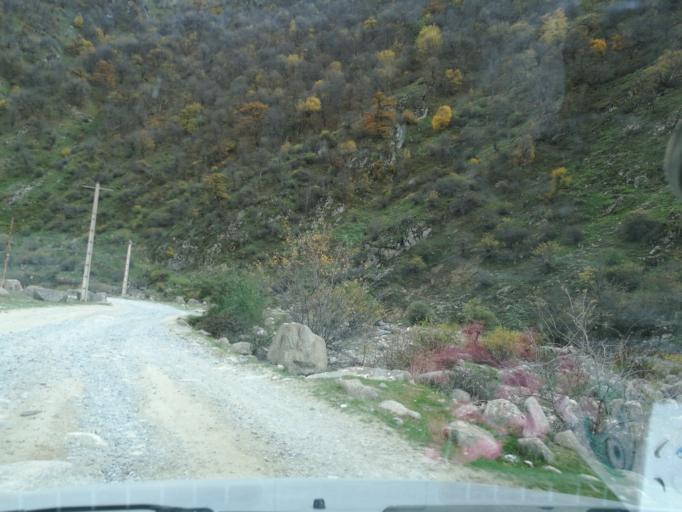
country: IR
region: Mazandaran
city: `Abbasabad
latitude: 36.4382
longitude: 51.0652
